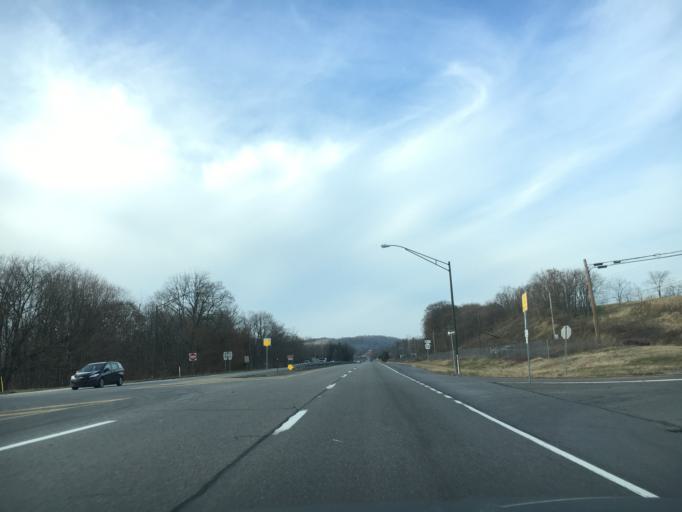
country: US
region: Pennsylvania
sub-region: Montour County
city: Danville
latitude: 40.9861
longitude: -76.6314
